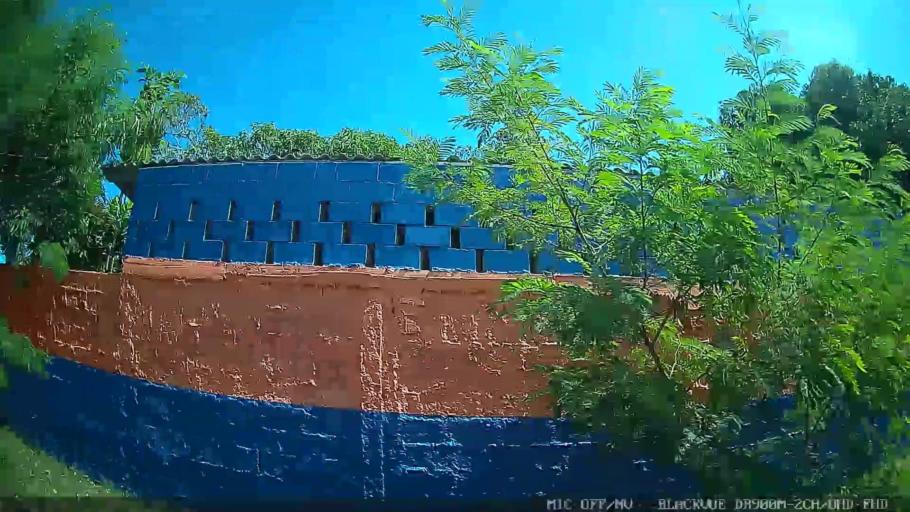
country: BR
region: Sao Paulo
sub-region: Peruibe
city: Peruibe
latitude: -24.3099
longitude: -46.9975
